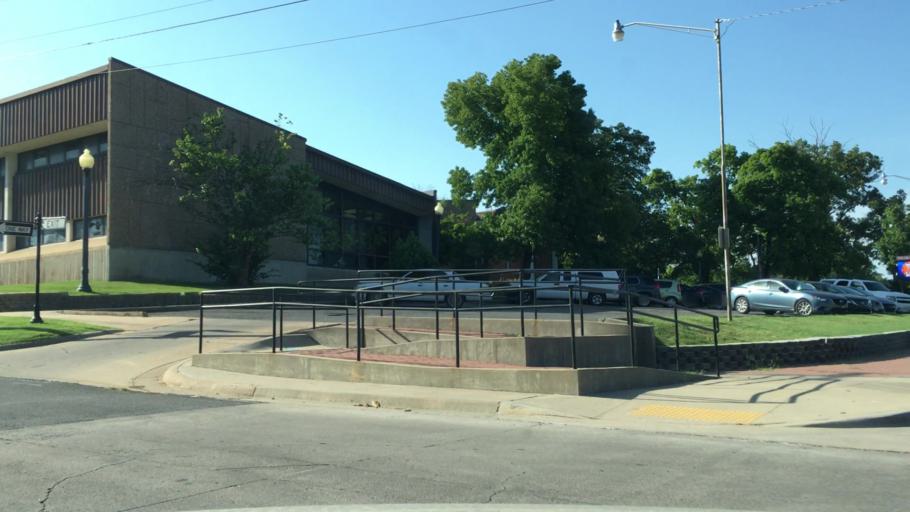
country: US
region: Oklahoma
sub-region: Cherokee County
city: Tahlequah
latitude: 35.9127
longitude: -94.9729
